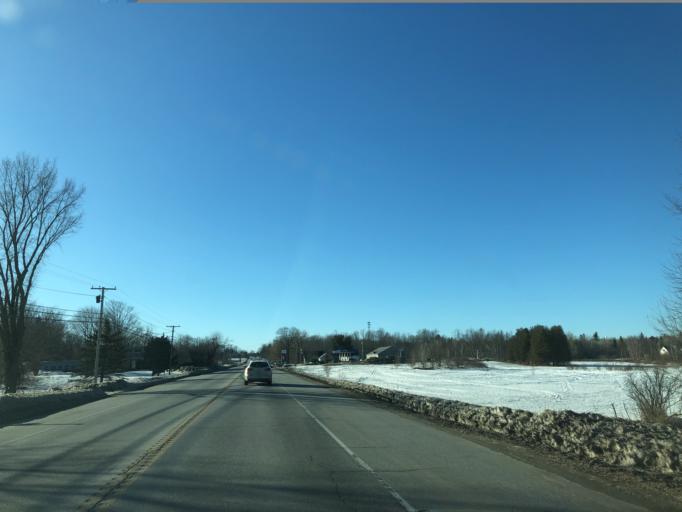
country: US
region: Maine
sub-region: Penobscot County
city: Kenduskeag
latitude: 44.9844
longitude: -69.0043
